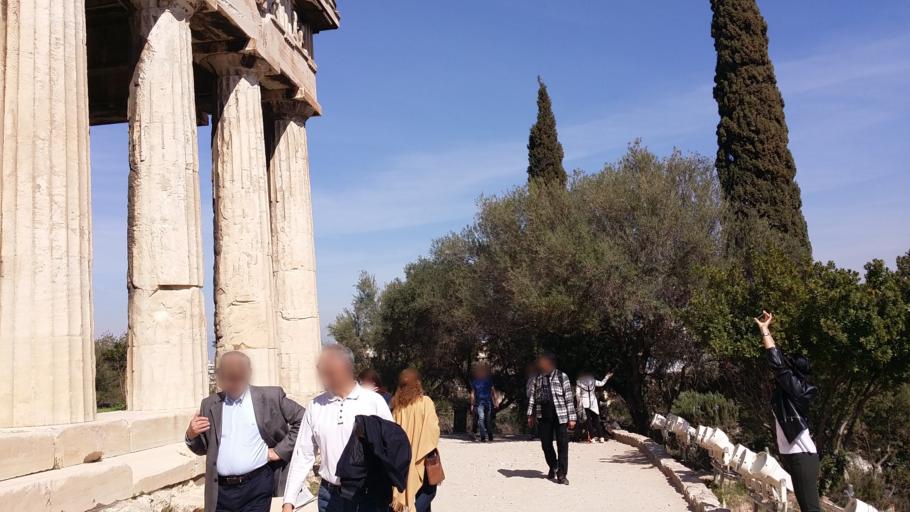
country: GR
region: Attica
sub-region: Nomarchia Athinas
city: Athens
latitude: 37.9754
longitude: 23.7216
